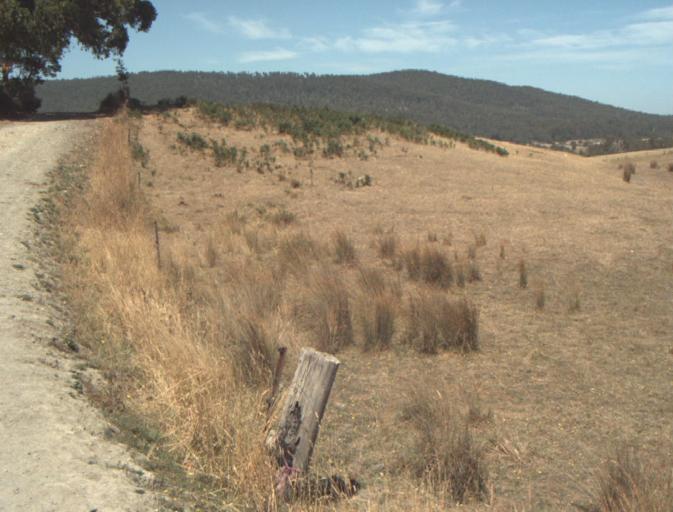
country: AU
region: Tasmania
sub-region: Launceston
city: Mayfield
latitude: -41.2503
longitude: 147.1741
